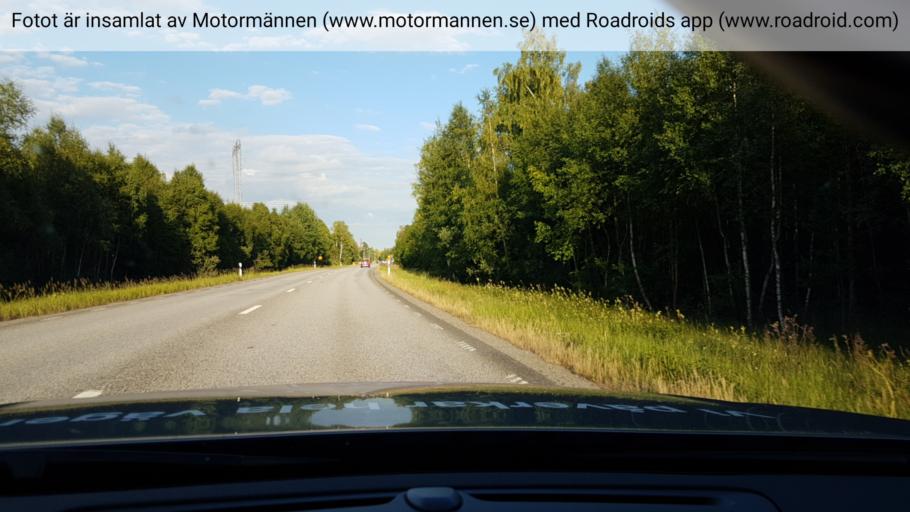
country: SE
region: Uppsala
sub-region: Enkopings Kommun
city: Orsundsbro
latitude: 59.8887
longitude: 17.1843
